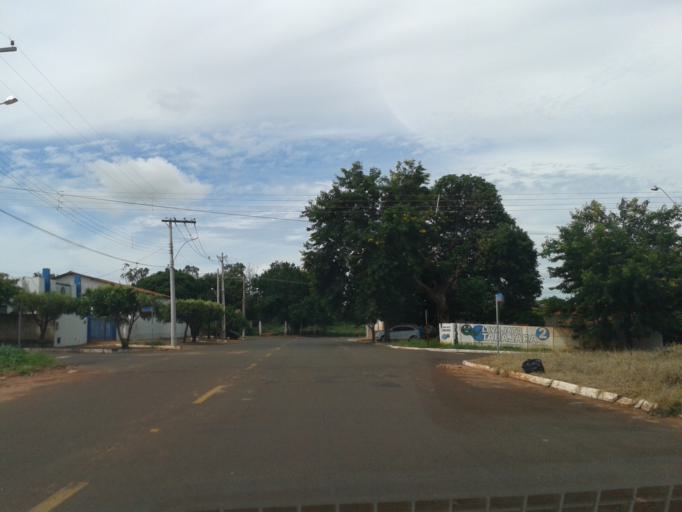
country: BR
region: Minas Gerais
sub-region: Santa Vitoria
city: Santa Vitoria
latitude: -18.8450
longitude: -50.1279
